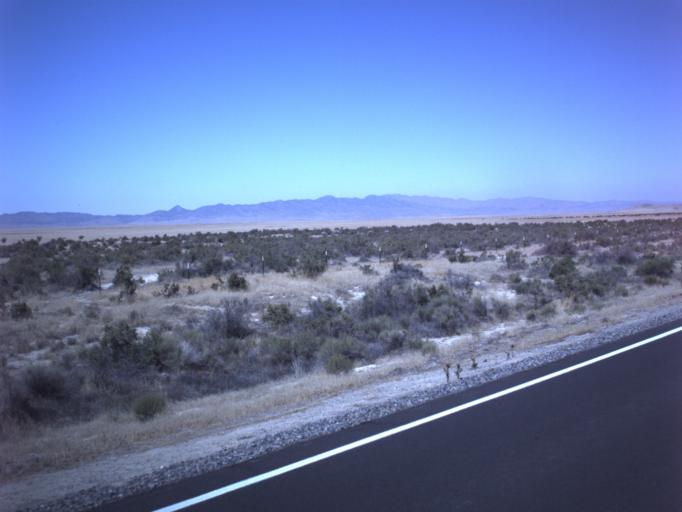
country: US
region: Utah
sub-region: Tooele County
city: Grantsville
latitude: 40.3028
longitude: -112.7429
